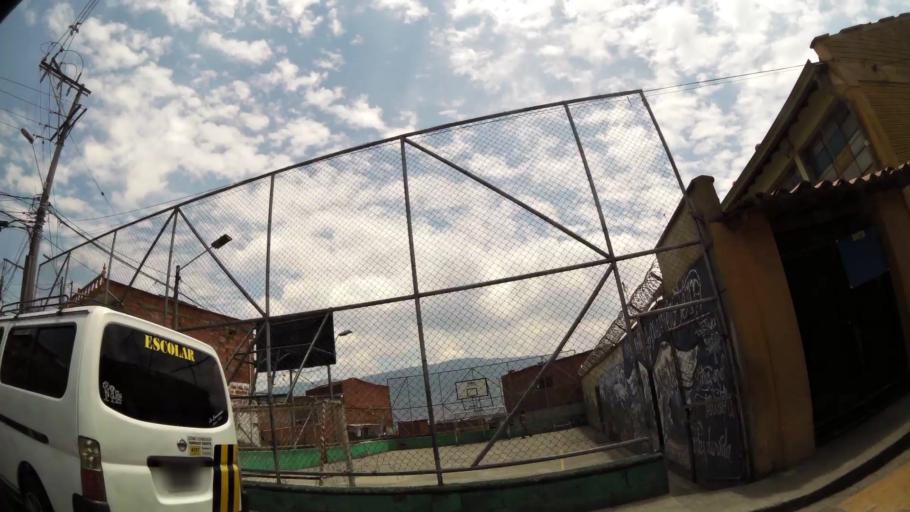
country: CO
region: Antioquia
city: Medellin
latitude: 6.2950
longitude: -75.5836
